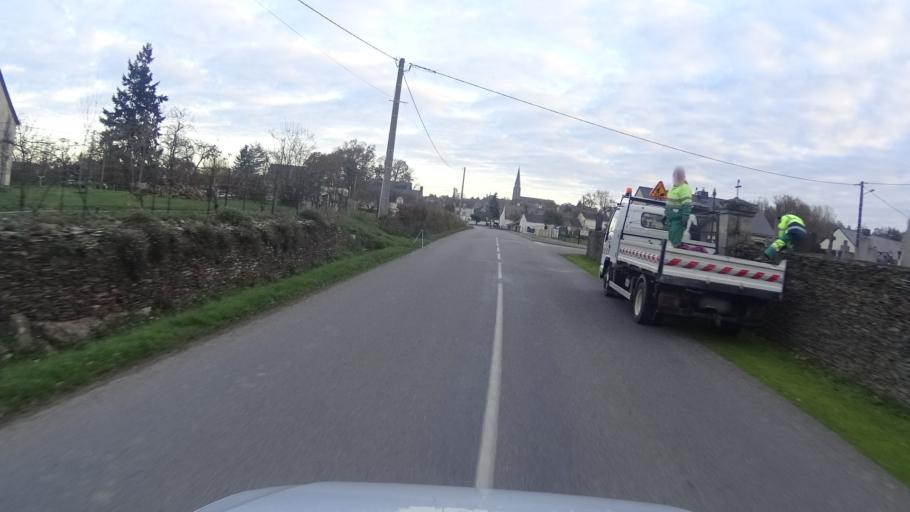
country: FR
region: Brittany
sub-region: Departement d'Ille-et-Vilaine
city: Langon
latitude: 47.6928
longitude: -1.8686
